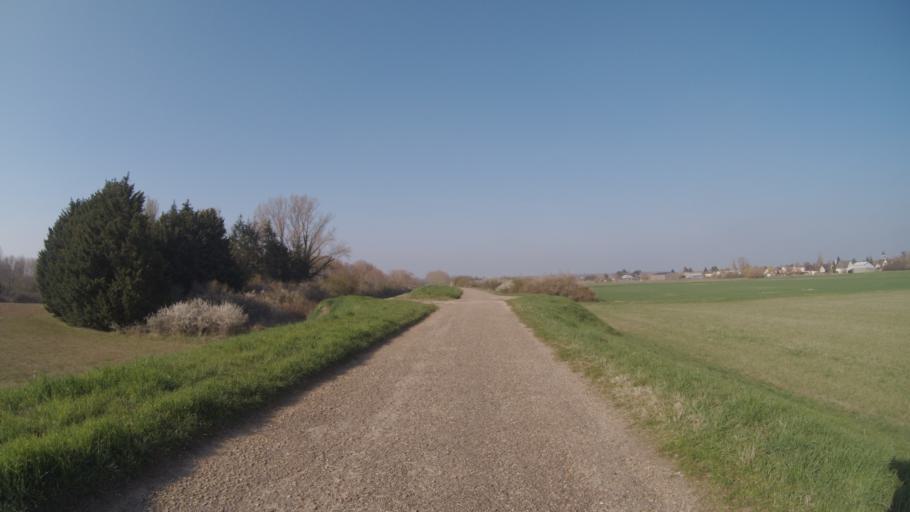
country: FR
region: Centre
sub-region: Departement du Loiret
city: Sandillon
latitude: 47.8692
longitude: 2.0368
